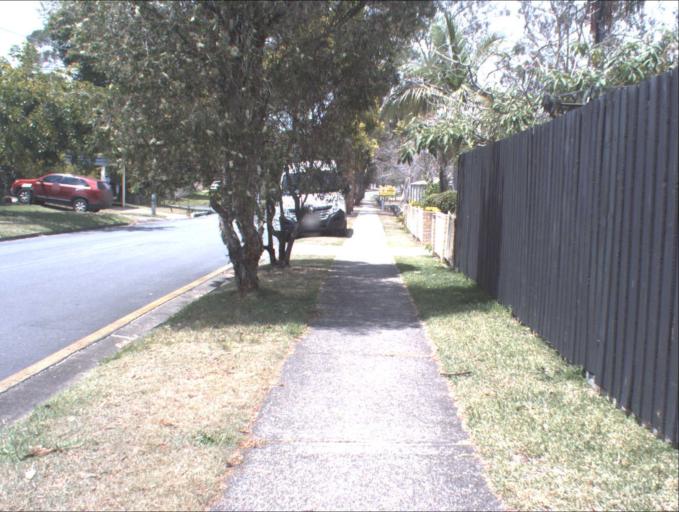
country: AU
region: Queensland
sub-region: Logan
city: Springwood
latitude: -27.6191
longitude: 153.1359
